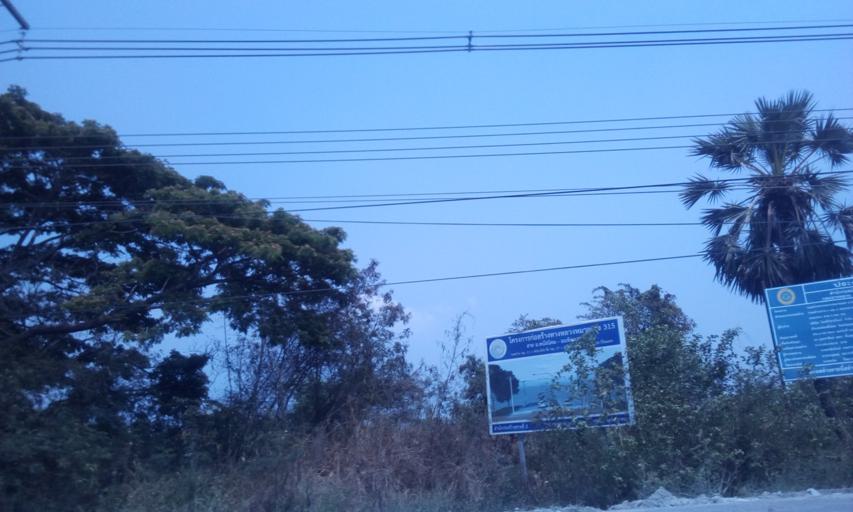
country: TH
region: Chachoengsao
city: Ban Pho
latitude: 13.5649
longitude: 101.1321
